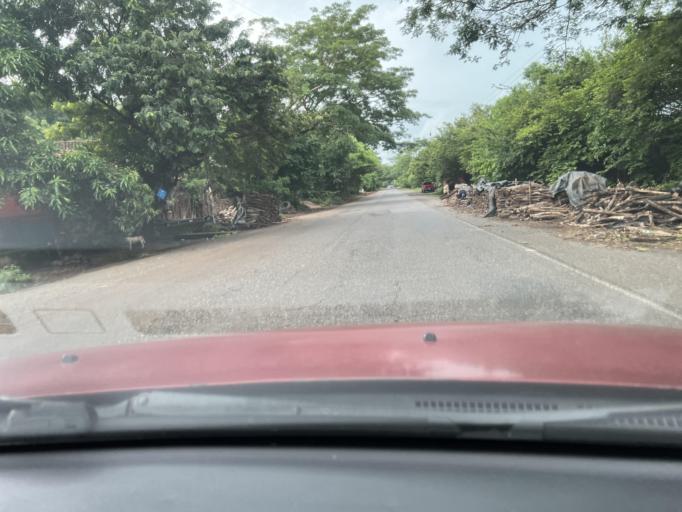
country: SV
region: La Union
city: San Alejo
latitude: 13.4059
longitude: -87.8928
